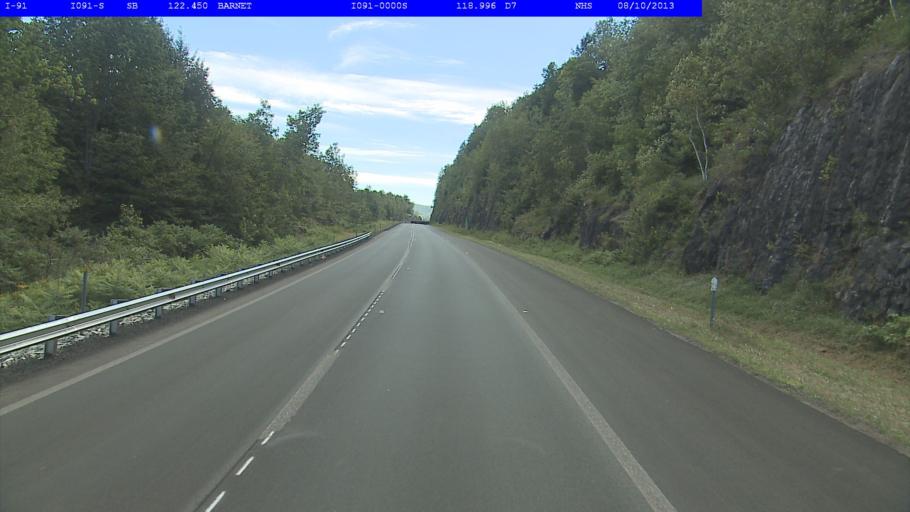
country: US
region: Vermont
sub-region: Caledonia County
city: Saint Johnsbury
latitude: 44.3168
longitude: -72.0383
